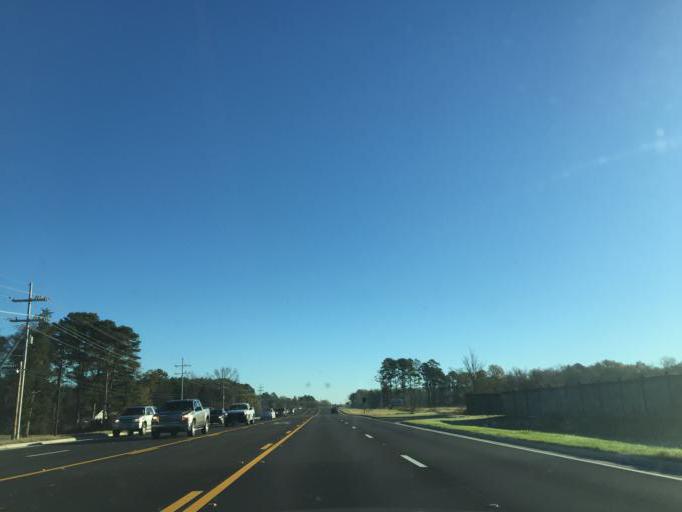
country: US
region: Mississippi
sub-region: Rankin County
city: Flowood
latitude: 32.3196
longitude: -90.1267
